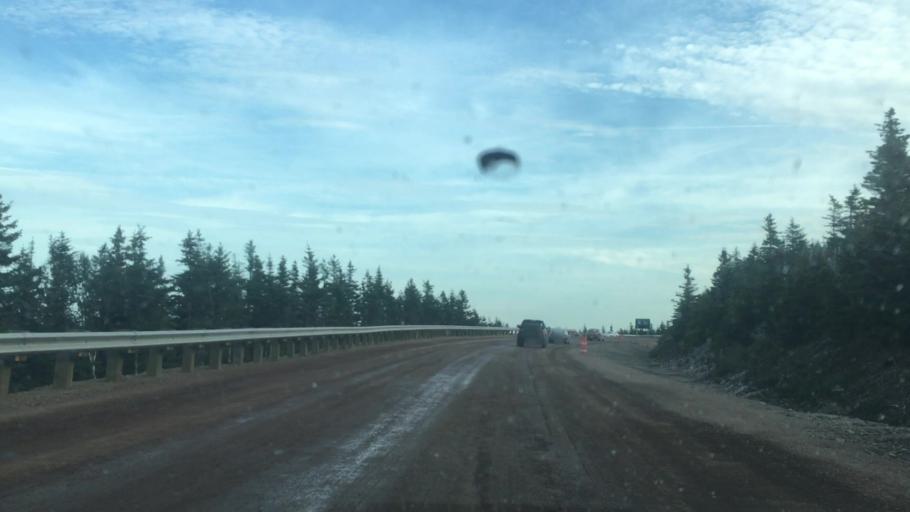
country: CA
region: Nova Scotia
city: Sydney Mines
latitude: 46.8049
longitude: -60.8439
